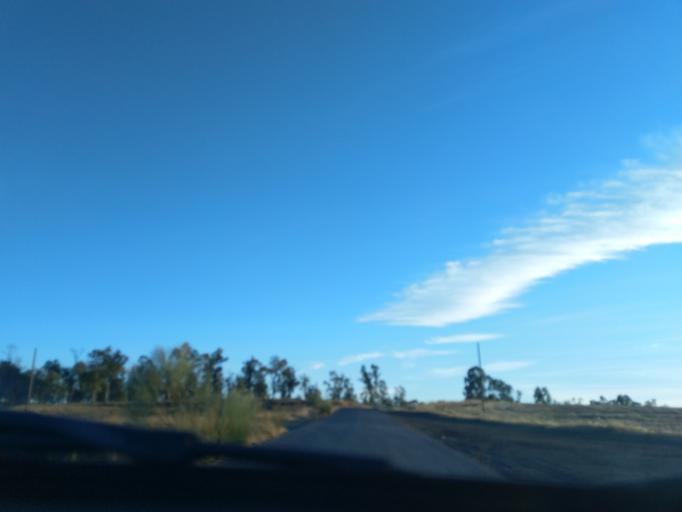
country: ES
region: Extremadura
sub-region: Provincia de Badajoz
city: Berlanga
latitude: 38.2735
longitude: -5.8209
